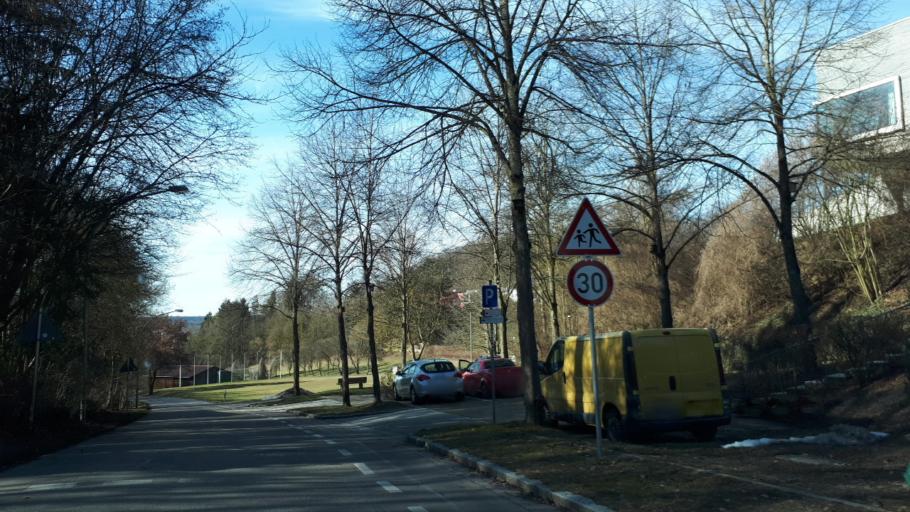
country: DE
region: Bavaria
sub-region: Upper Palatinate
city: Pentling
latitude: 48.9819
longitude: 12.0564
